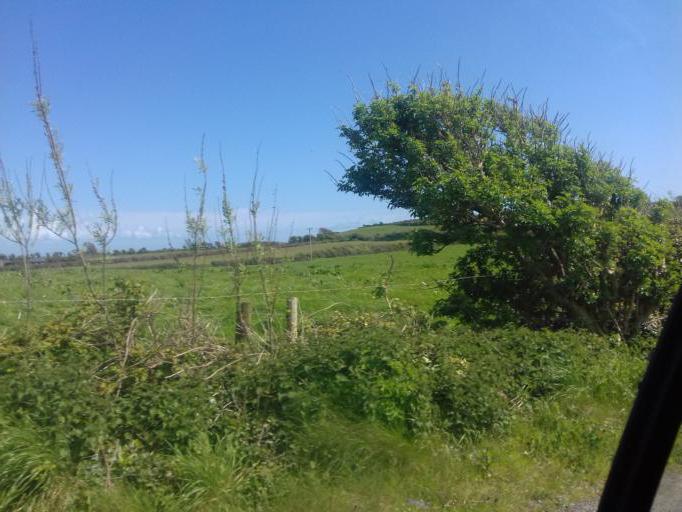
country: IE
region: Munster
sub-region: Waterford
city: Dunmore East
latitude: 52.1793
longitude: -6.8949
